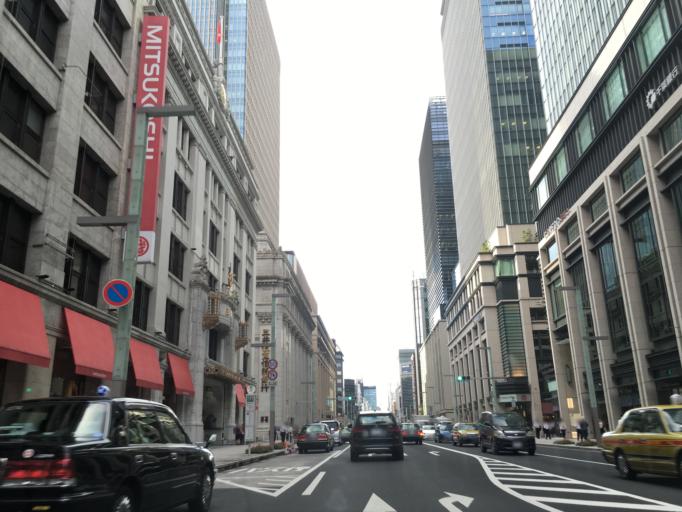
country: JP
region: Tokyo
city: Tokyo
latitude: 35.6857
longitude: 139.7742
